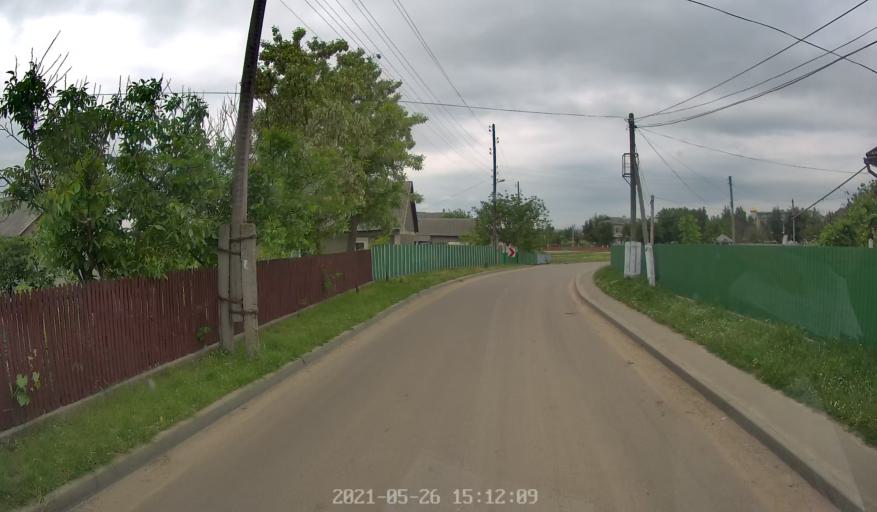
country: MD
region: Hincesti
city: Dancu
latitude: 46.6640
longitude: 28.3292
